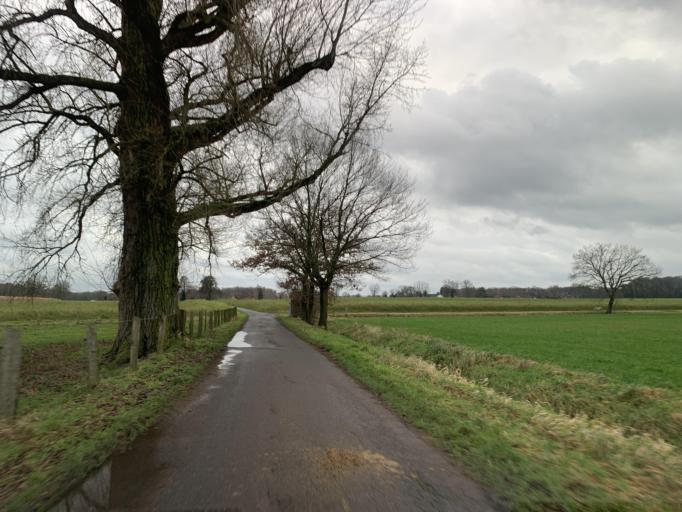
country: DE
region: North Rhine-Westphalia
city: Oer-Erkenschwick
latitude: 51.6858
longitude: 7.3049
